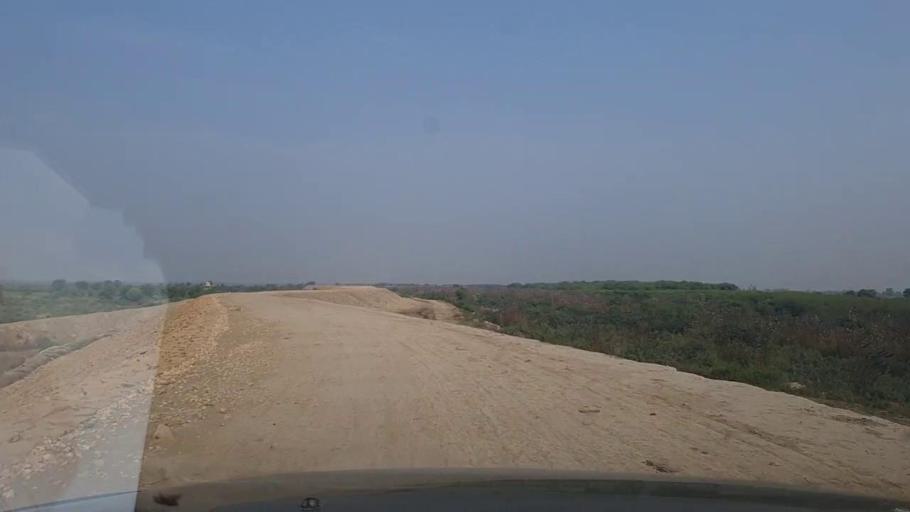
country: PK
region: Sindh
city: Bulri
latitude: 24.9609
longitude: 68.2921
